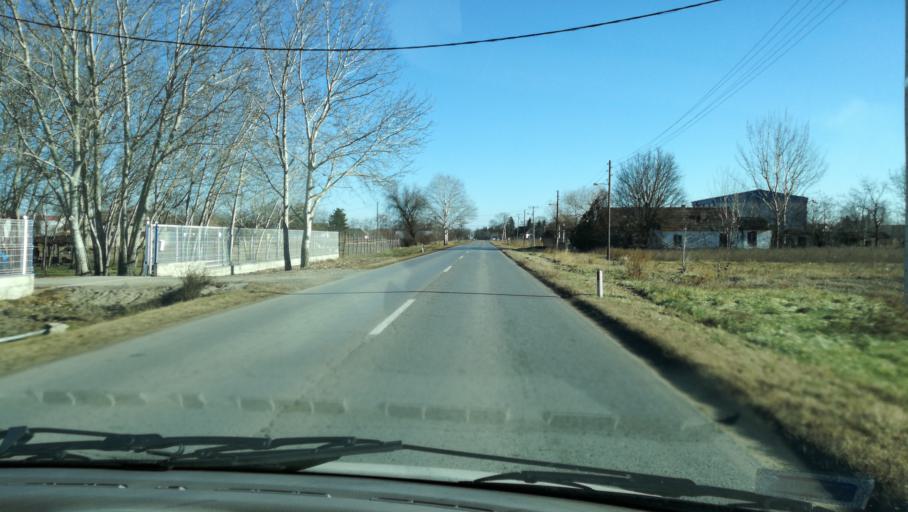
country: HU
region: Csongrad
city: Morahalom
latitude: 46.1035
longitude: 19.8631
